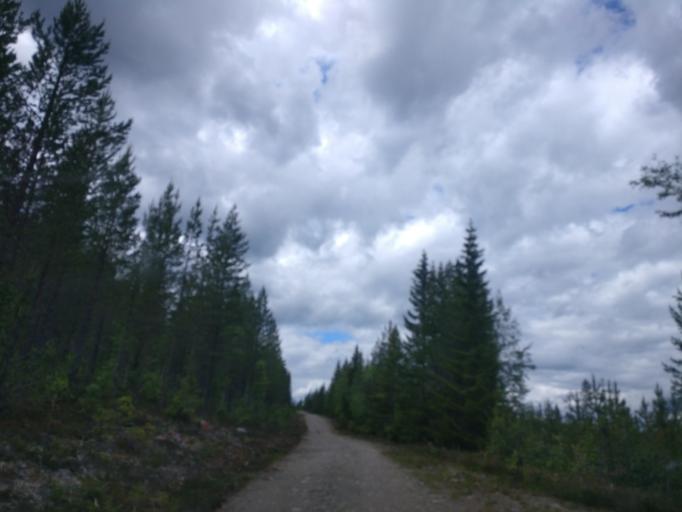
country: SE
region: Jaemtland
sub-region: Harjedalens Kommun
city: Sveg
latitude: 62.1968
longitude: 13.4120
